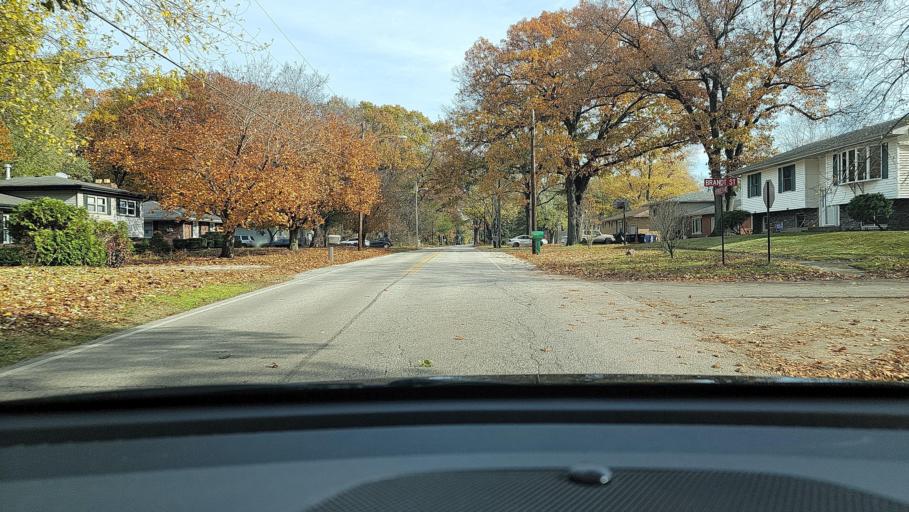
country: US
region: Indiana
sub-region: Porter County
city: Portage
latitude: 41.5796
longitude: -87.2045
